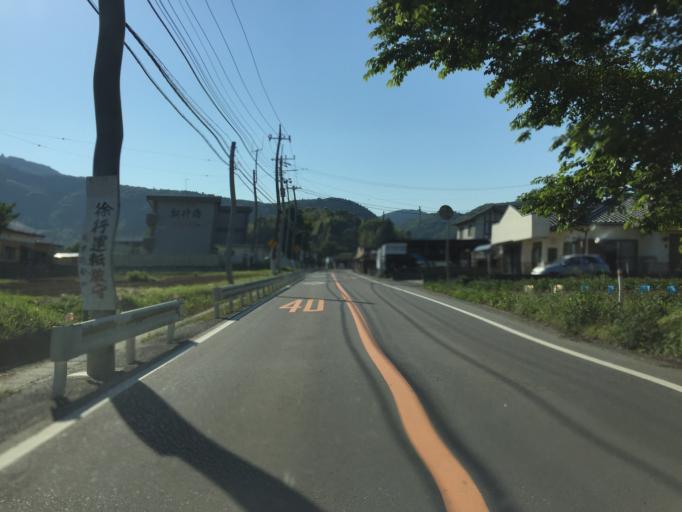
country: JP
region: Ibaraki
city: Kitaibaraki
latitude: 36.8555
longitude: 140.7293
